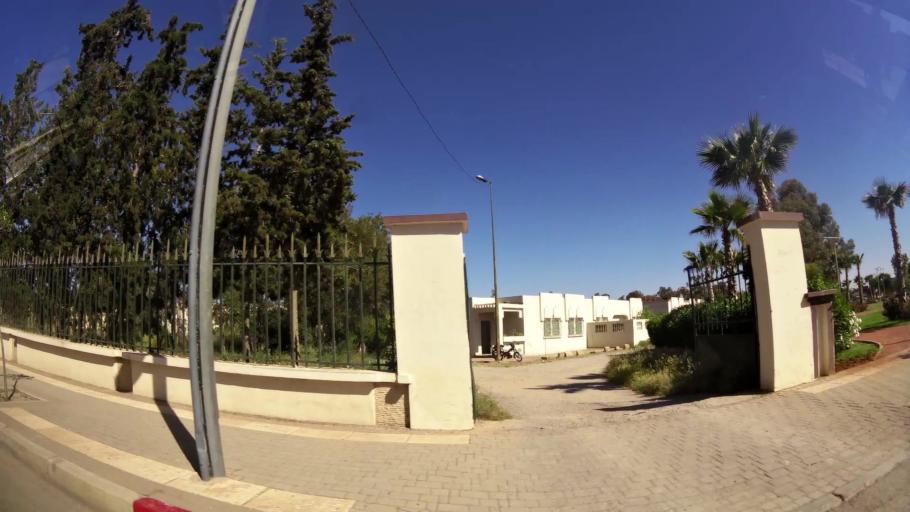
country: MA
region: Oriental
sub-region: Oujda-Angad
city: Oujda
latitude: 34.7172
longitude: -1.9208
